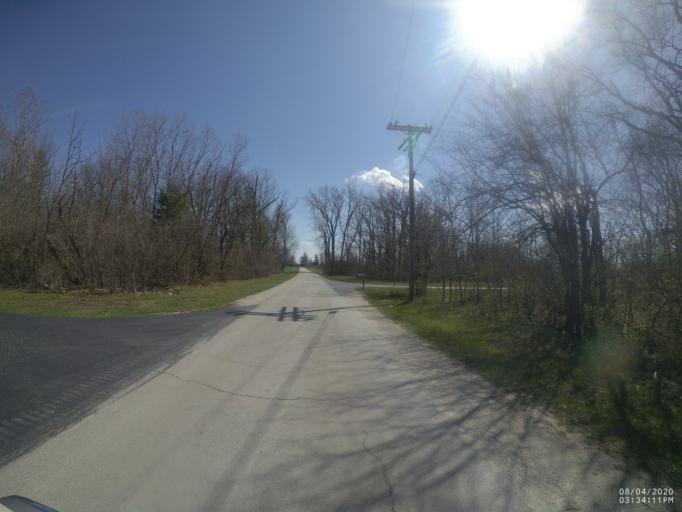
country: US
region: Ohio
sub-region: Sandusky County
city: Stony Prairie
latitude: 41.2650
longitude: -83.2573
